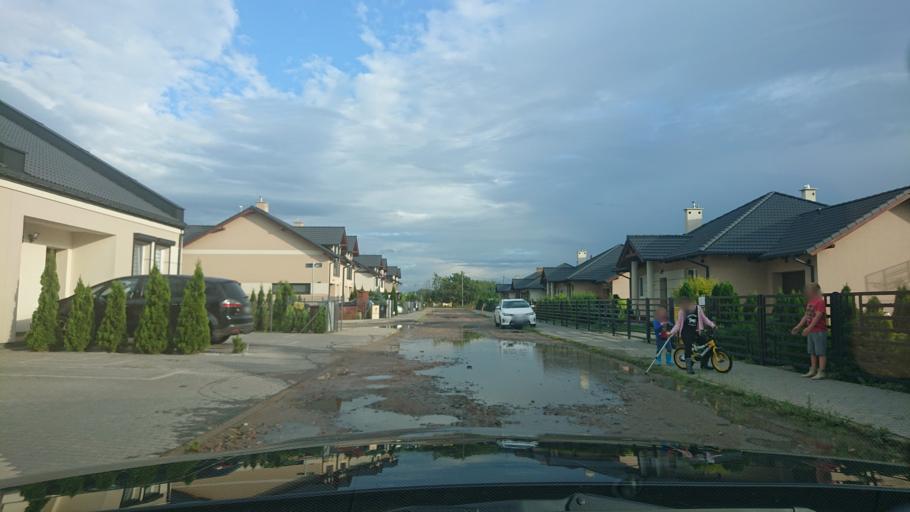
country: PL
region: Greater Poland Voivodeship
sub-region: Powiat gnieznienski
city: Gniezno
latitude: 52.5676
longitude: 17.6149
